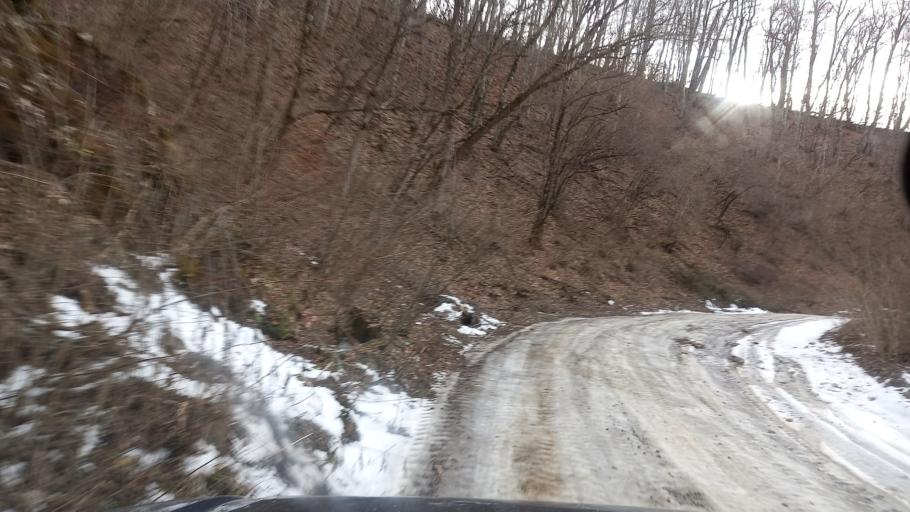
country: RU
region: Adygeya
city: Kamennomostskiy
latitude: 44.1517
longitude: 40.2983
